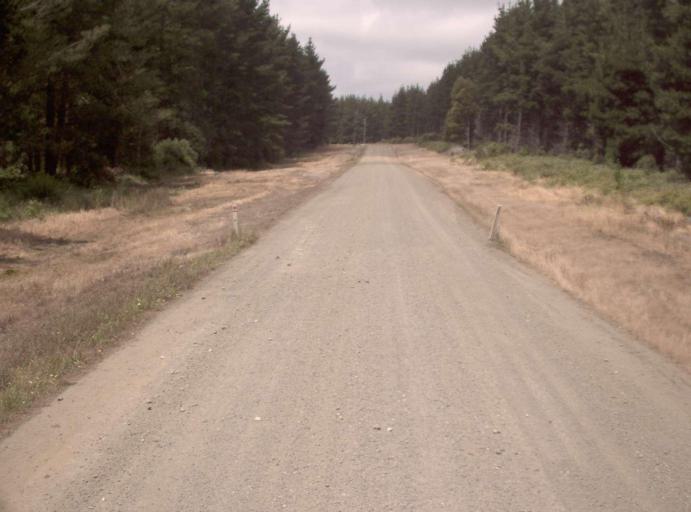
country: AU
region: Victoria
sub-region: Latrobe
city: Traralgon
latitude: -38.3993
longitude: 146.6515
